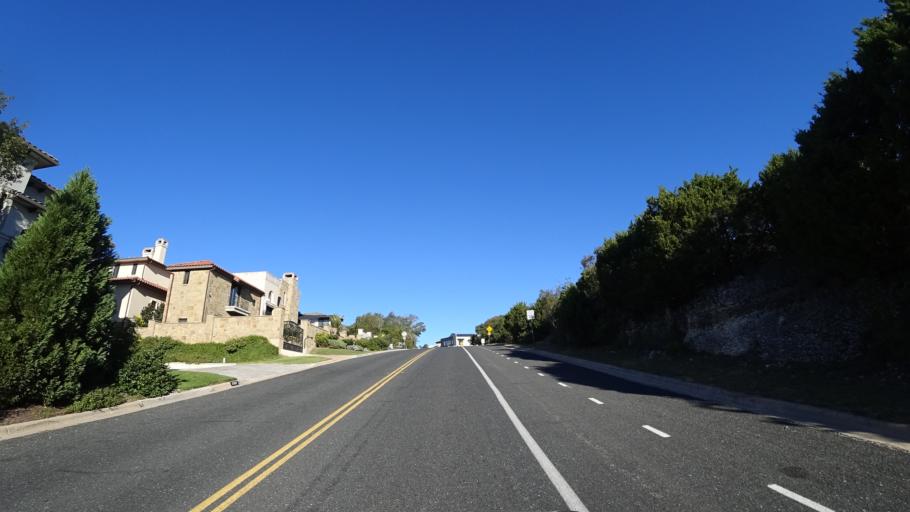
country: US
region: Texas
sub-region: Travis County
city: West Lake Hills
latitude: 30.3579
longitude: -97.8004
